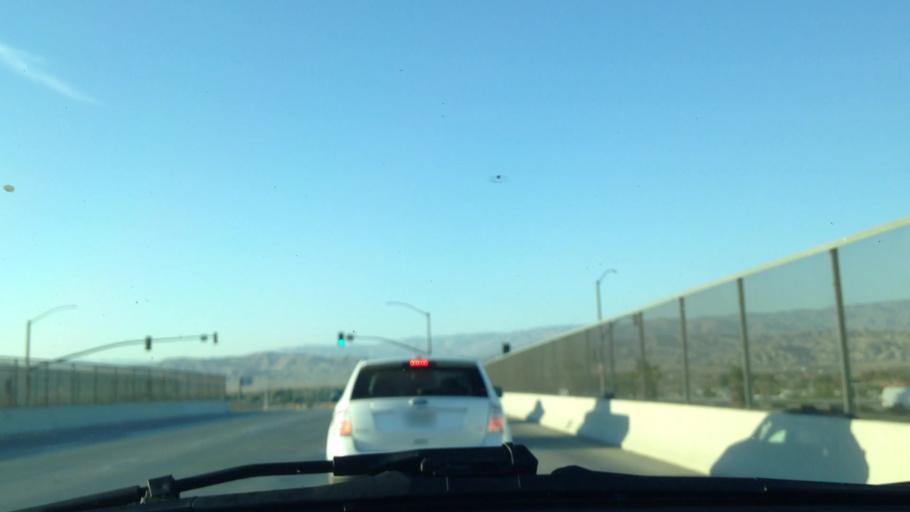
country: US
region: California
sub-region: Riverside County
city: Thousand Palms
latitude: 33.8049
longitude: -116.3881
